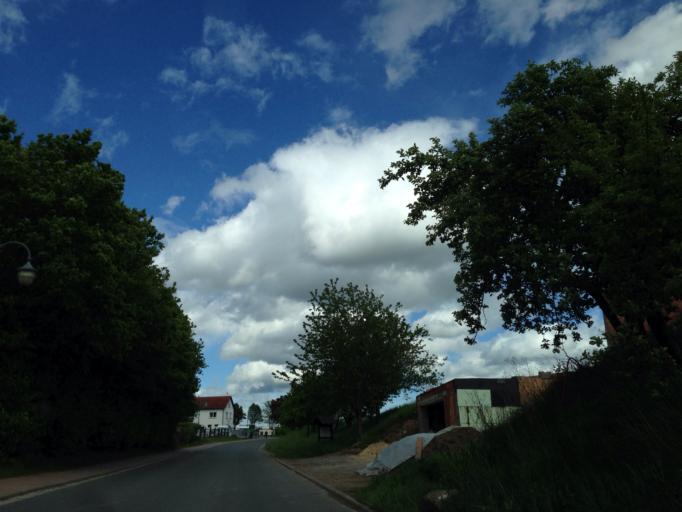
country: DE
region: Thuringia
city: Rudolstadt
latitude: 50.7762
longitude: 11.3610
